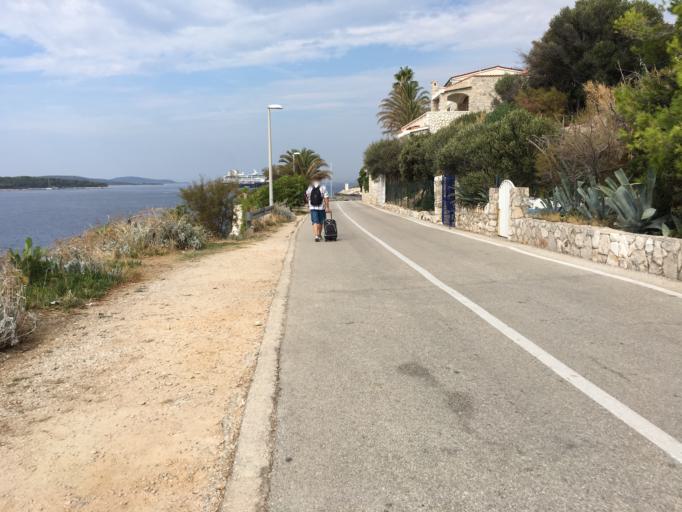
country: HR
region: Splitsko-Dalmatinska
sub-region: Grad Hvar
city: Hvar
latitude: 43.1637
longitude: 16.4433
